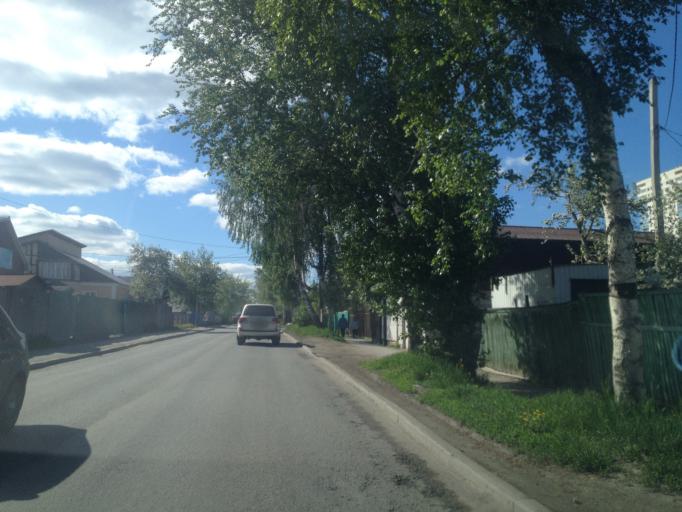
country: RU
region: Sverdlovsk
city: Sovkhoznyy
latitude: 56.8068
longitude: 60.5724
